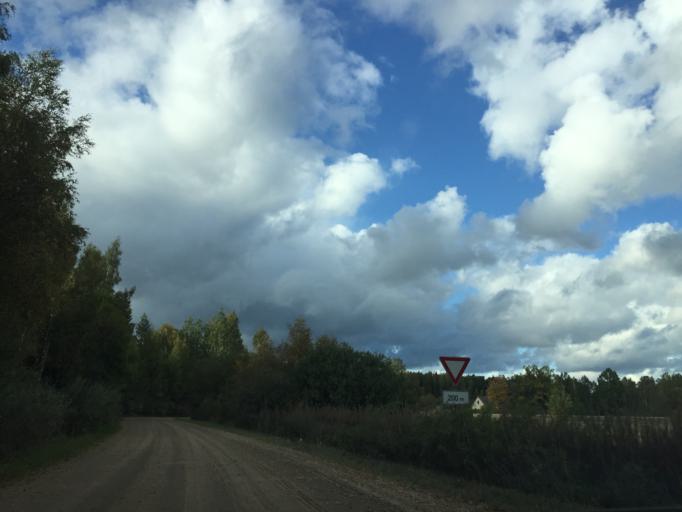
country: LV
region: Malpils
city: Malpils
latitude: 57.0318
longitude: 25.0510
